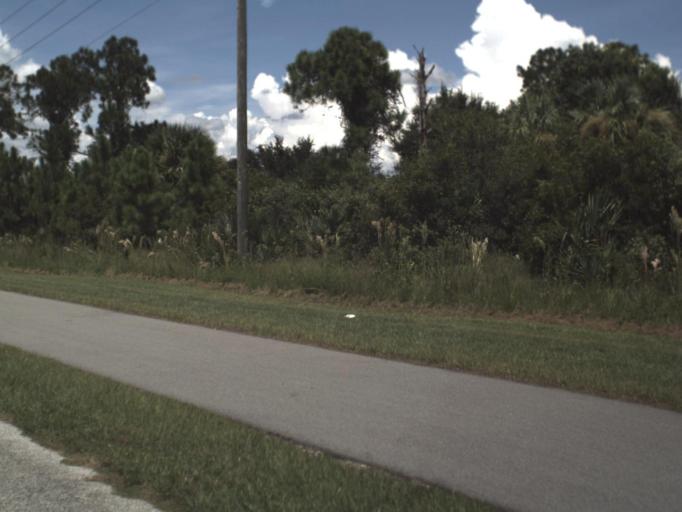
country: US
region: Florida
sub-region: Charlotte County
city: Charlotte Park
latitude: 26.8961
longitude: -82.0280
